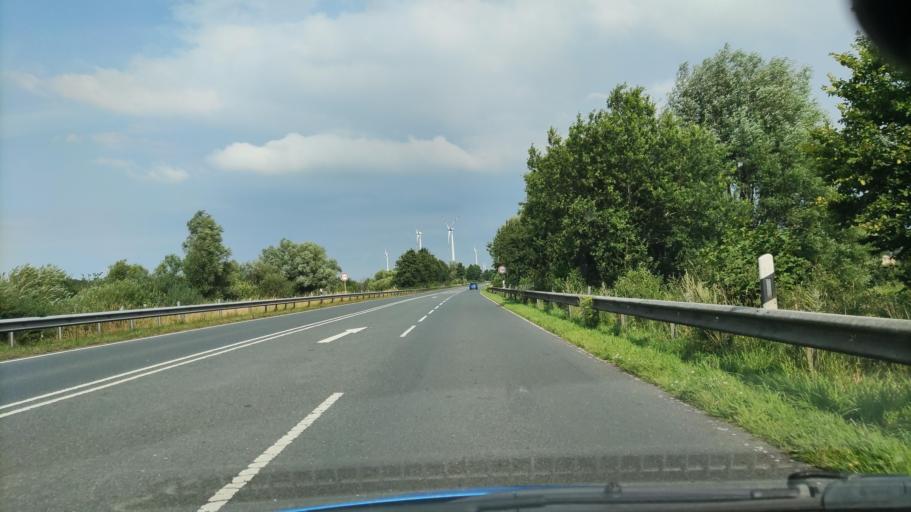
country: DE
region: Lower Saxony
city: Jever
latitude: 53.5852
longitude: 7.8909
